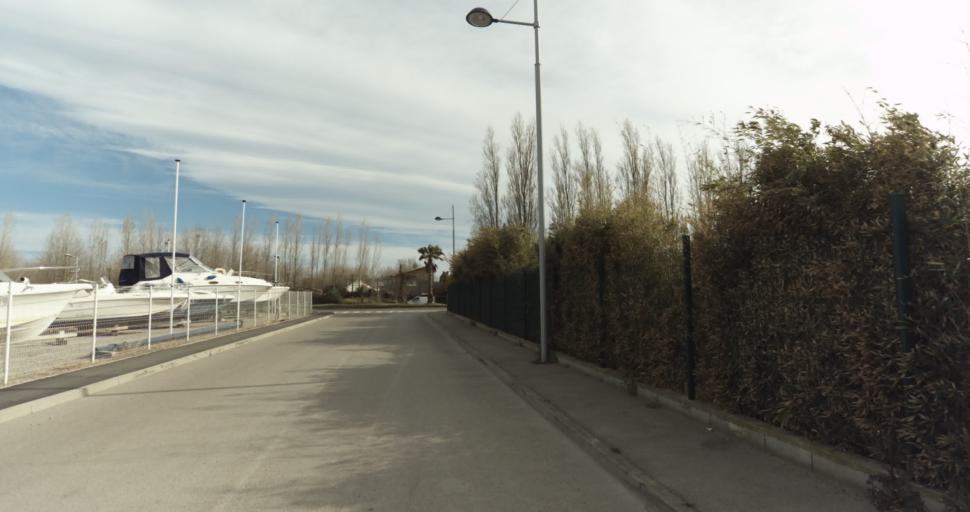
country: FR
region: Languedoc-Roussillon
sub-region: Departement de l'Herault
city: Marseillan
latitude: 43.3208
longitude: 3.5499
